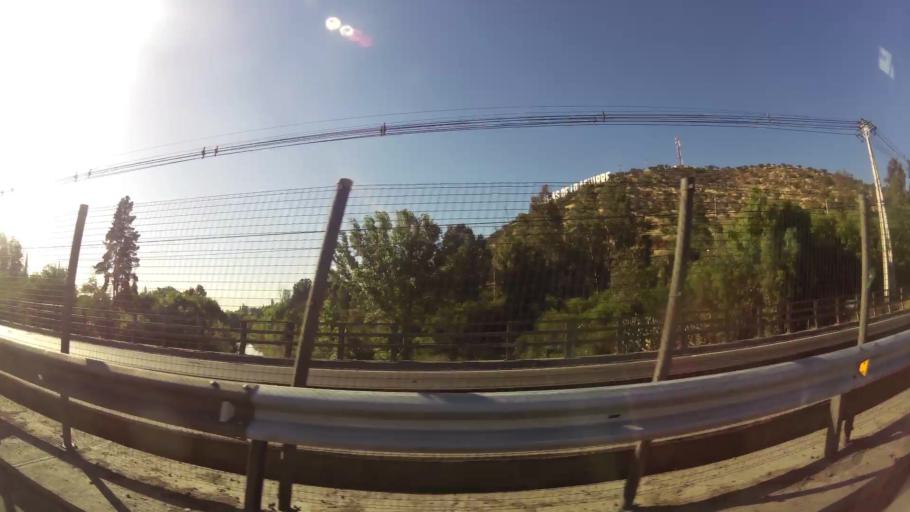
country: CL
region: Santiago Metropolitan
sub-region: Provincia de Santiago
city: Lo Prado
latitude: -33.4378
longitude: -70.8285
